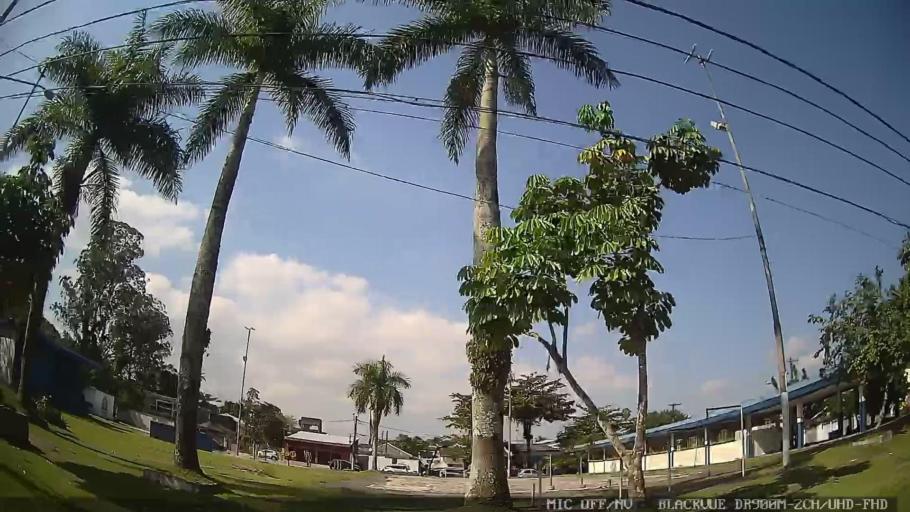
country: BR
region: Sao Paulo
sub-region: Santos
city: Santos
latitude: -23.9379
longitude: -46.3043
